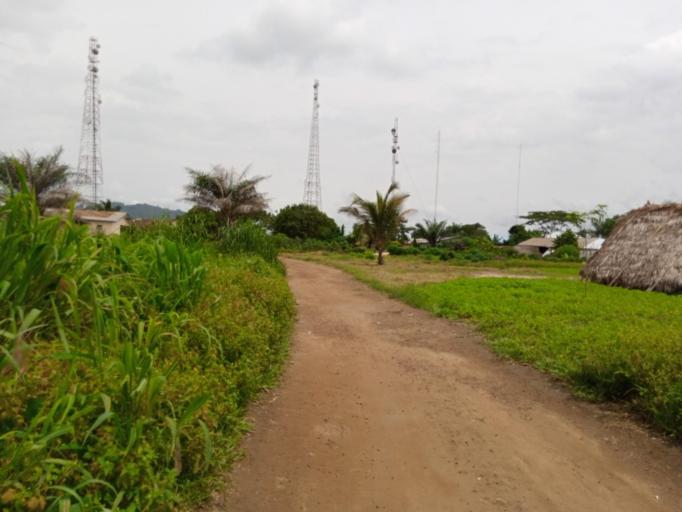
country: SL
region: Southern Province
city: Moyamba
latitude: 8.1677
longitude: -12.4182
